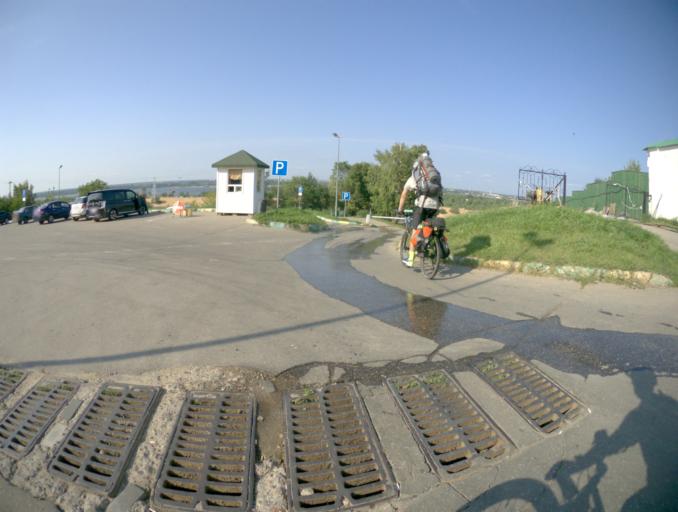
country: RU
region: Nizjnij Novgorod
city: Bor
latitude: 56.3237
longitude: 44.0470
